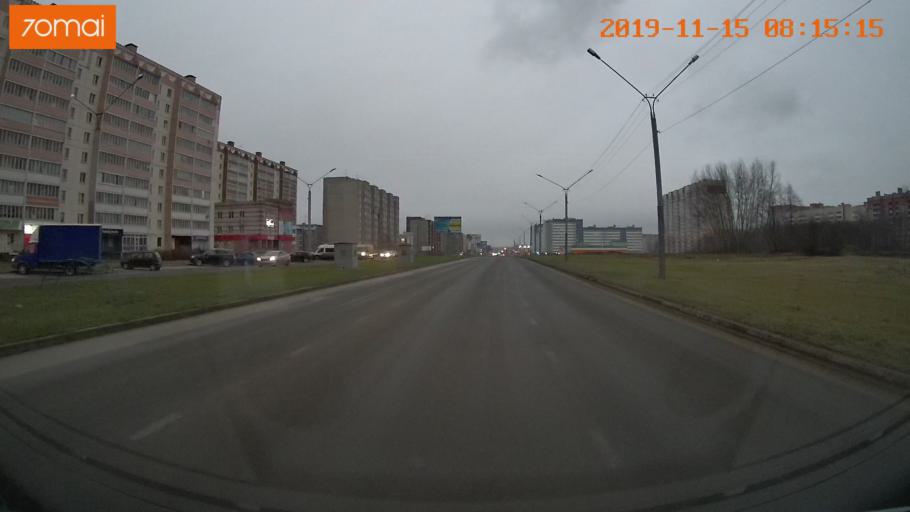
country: RU
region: Vologda
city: Cherepovets
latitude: 59.0808
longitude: 37.9234
